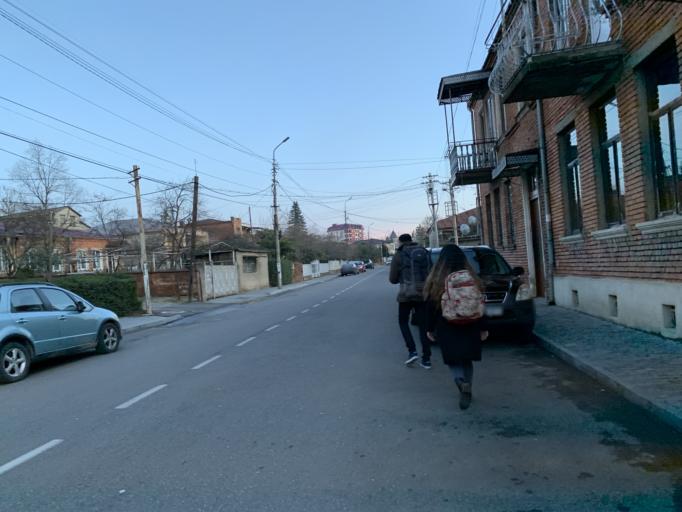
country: GE
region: Imereti
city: Kutaisi
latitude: 42.2683
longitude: 42.7137
